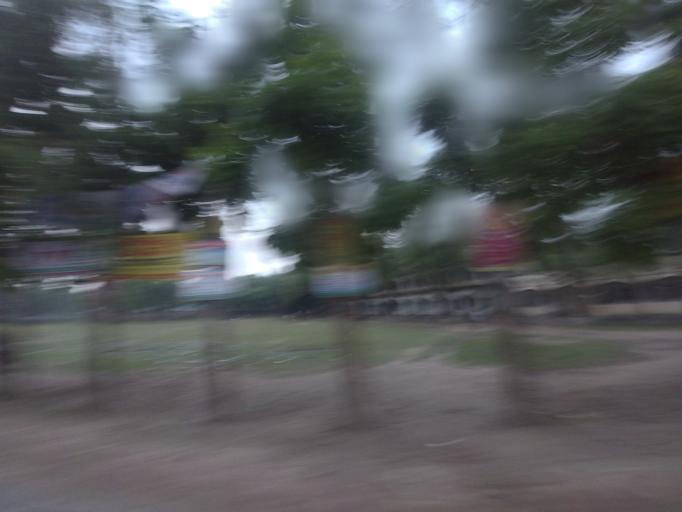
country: BD
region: Rajshahi
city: Sirajganj
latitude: 24.3191
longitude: 89.6490
